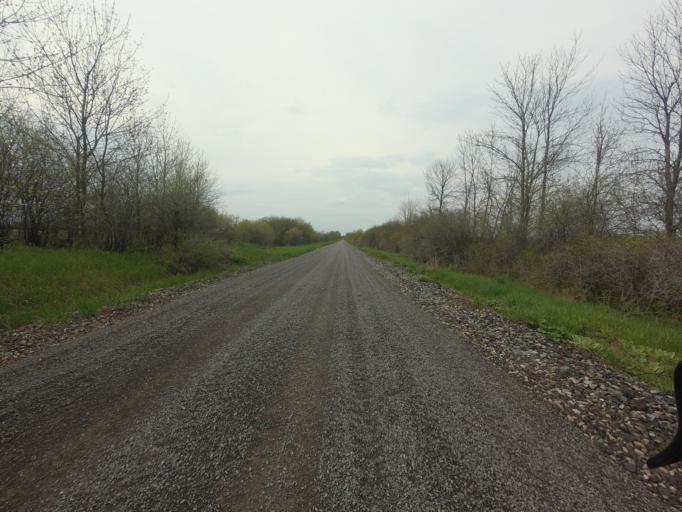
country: CA
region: Ontario
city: Carleton Place
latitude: 45.1947
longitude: -76.1642
